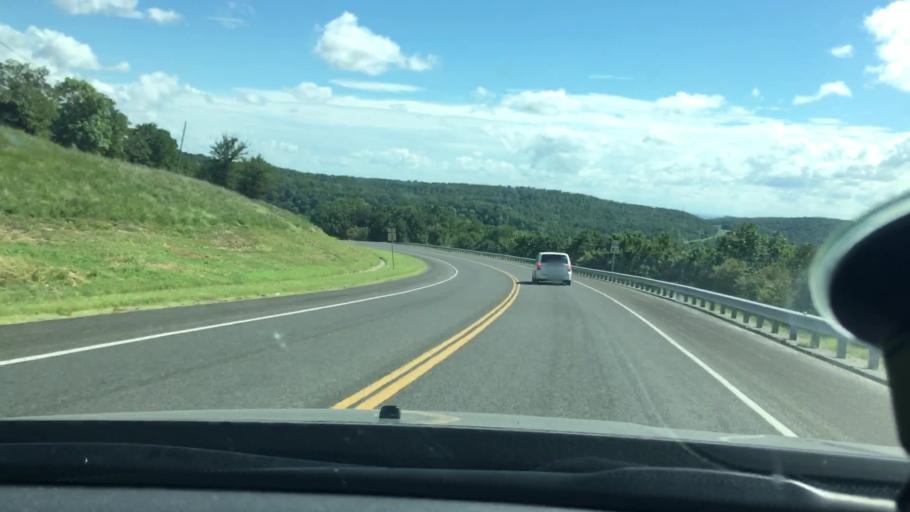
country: US
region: Oklahoma
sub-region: Sequoyah County
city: Vian
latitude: 35.5468
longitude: -94.9699
